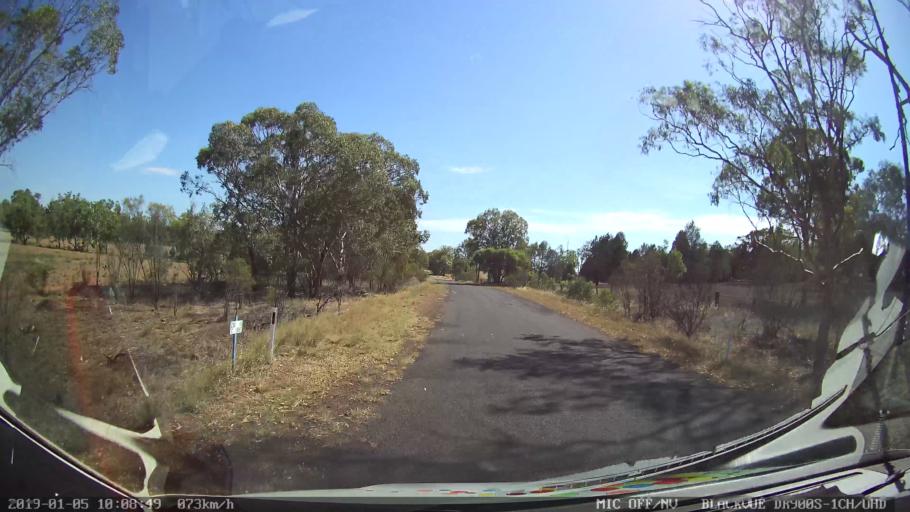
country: AU
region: New South Wales
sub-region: Gilgandra
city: Gilgandra
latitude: -31.6374
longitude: 148.8823
